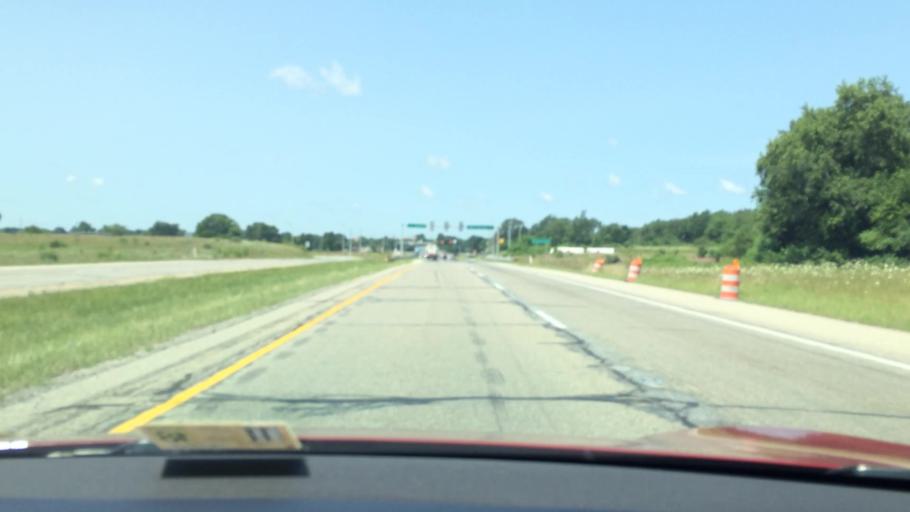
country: US
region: Indiana
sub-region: LaPorte County
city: Hudson Lake
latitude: 41.6729
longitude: -86.5856
